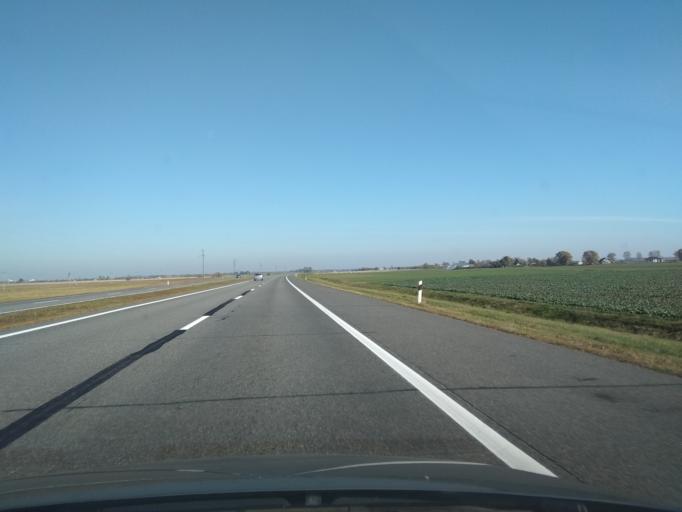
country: BY
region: Brest
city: Byaroza
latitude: 52.4754
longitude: 24.9410
